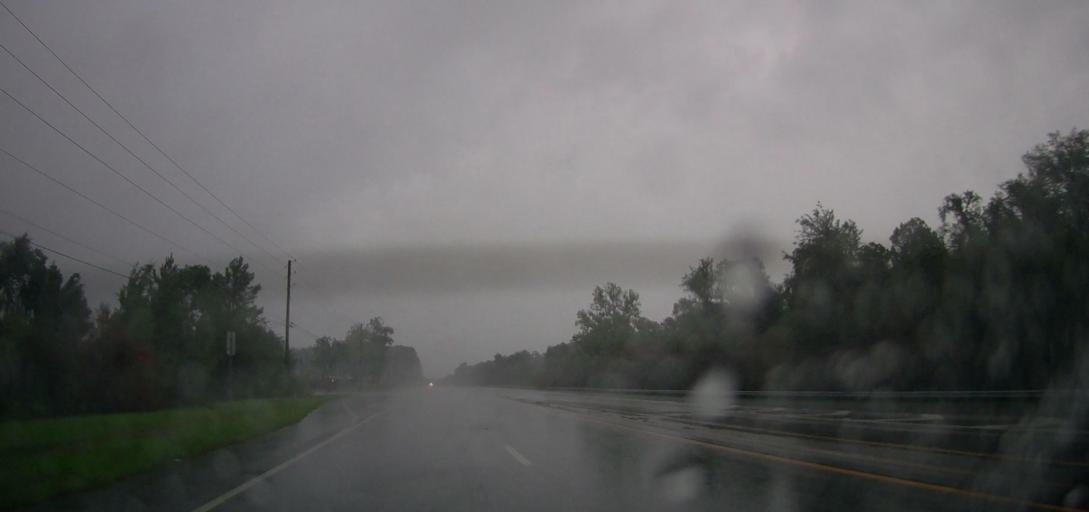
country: US
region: Georgia
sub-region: Clinch County
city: Homerville
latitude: 31.0595
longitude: -82.6864
